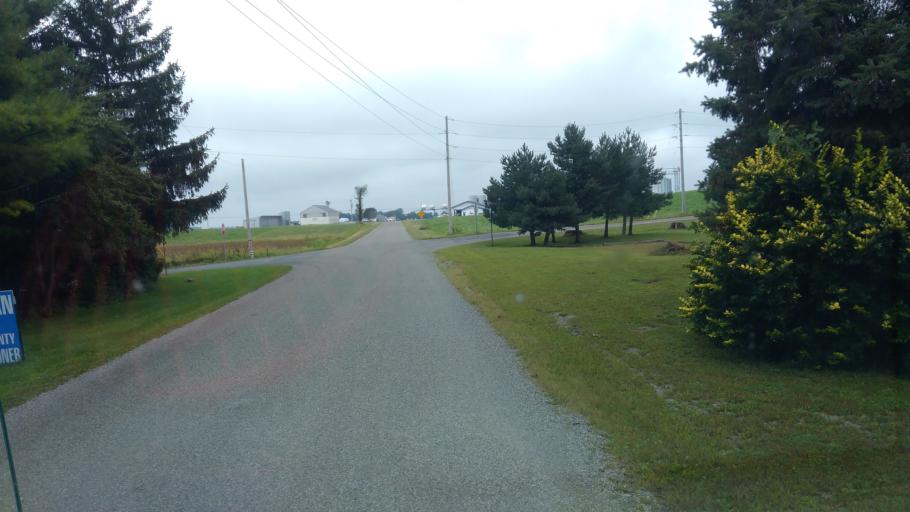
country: US
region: Ohio
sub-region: Hardin County
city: Kenton
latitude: 40.5773
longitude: -83.6821
